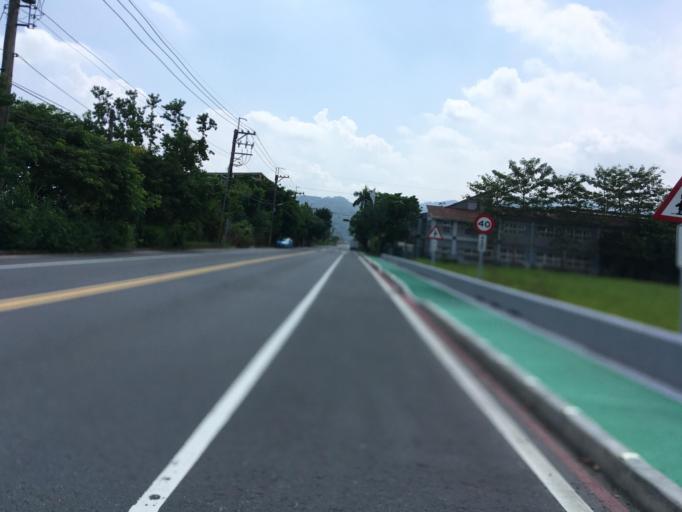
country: TW
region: Taiwan
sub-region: Yilan
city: Yilan
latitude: 24.6807
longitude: 121.6889
